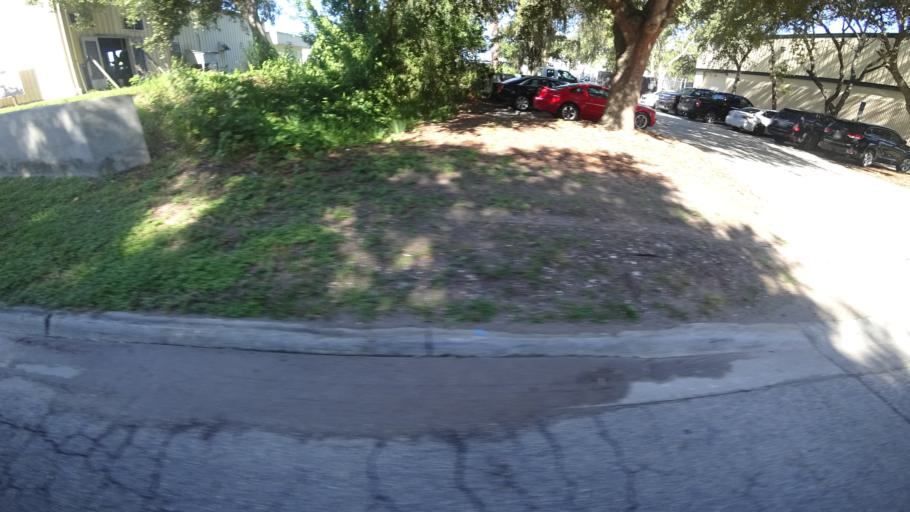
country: US
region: Florida
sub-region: Manatee County
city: Whitfield
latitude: 27.4237
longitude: -82.5342
